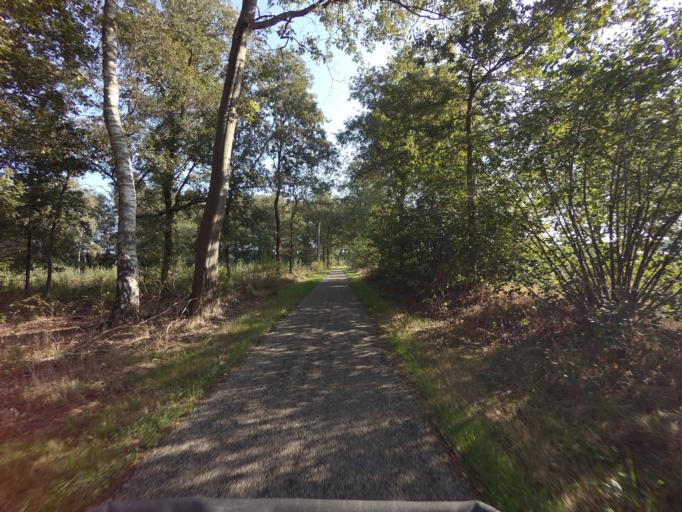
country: NL
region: Overijssel
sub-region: Gemeente Raalte
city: Raalte
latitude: 52.3117
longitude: 6.2762
